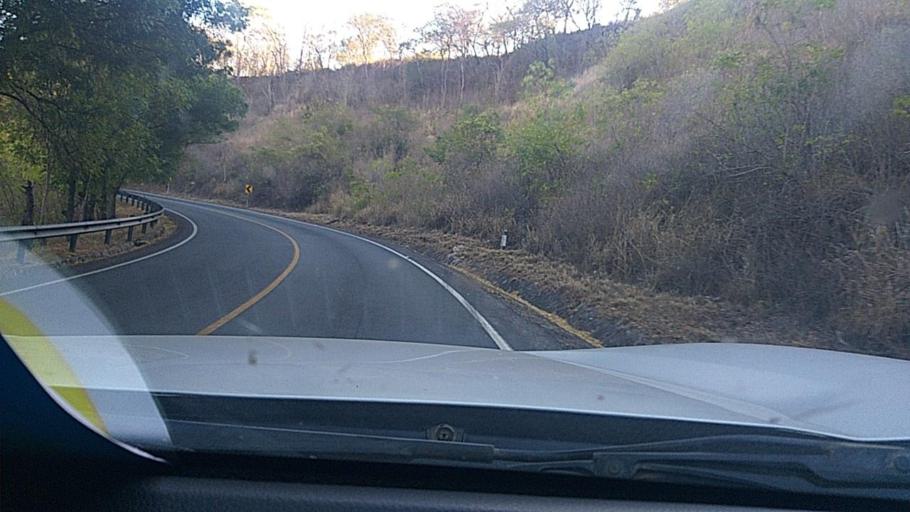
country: NI
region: Esteli
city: Condega
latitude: 13.2662
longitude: -86.3553
